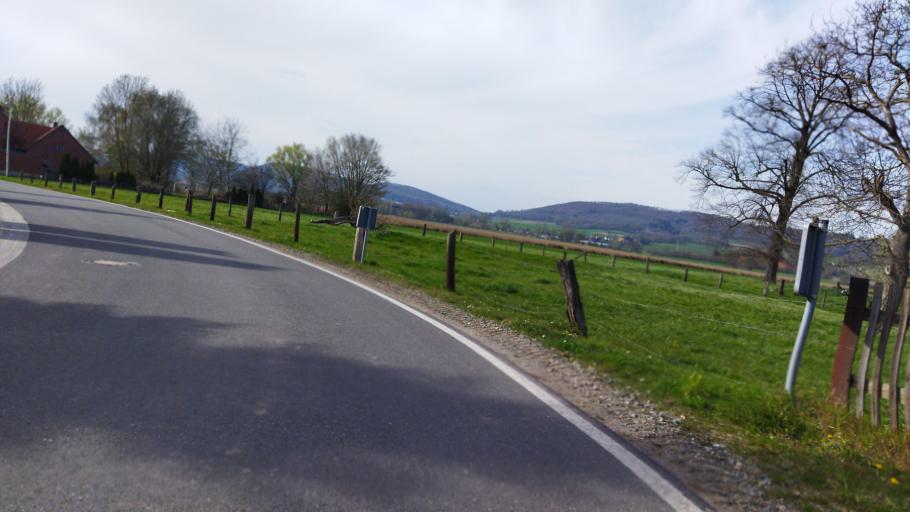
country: DE
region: Lower Saxony
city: Buchholz
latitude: 52.1860
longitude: 9.1507
